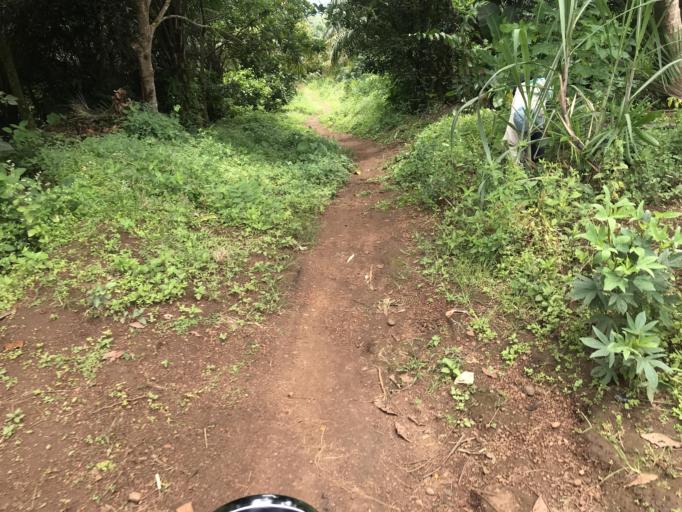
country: GN
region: Nzerekore
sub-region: Prefecture de Guekedou
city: Gueckedou
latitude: 8.4975
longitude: -10.3239
